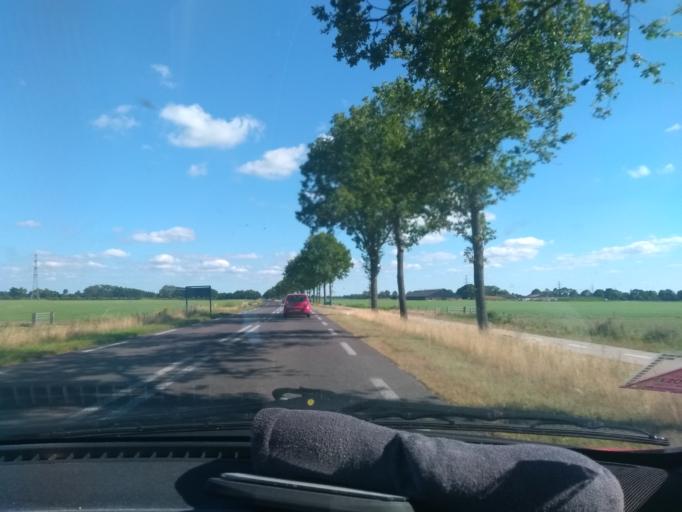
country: NL
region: Drenthe
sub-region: Gemeente Tynaarlo
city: Vries
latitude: 53.1228
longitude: 6.5046
